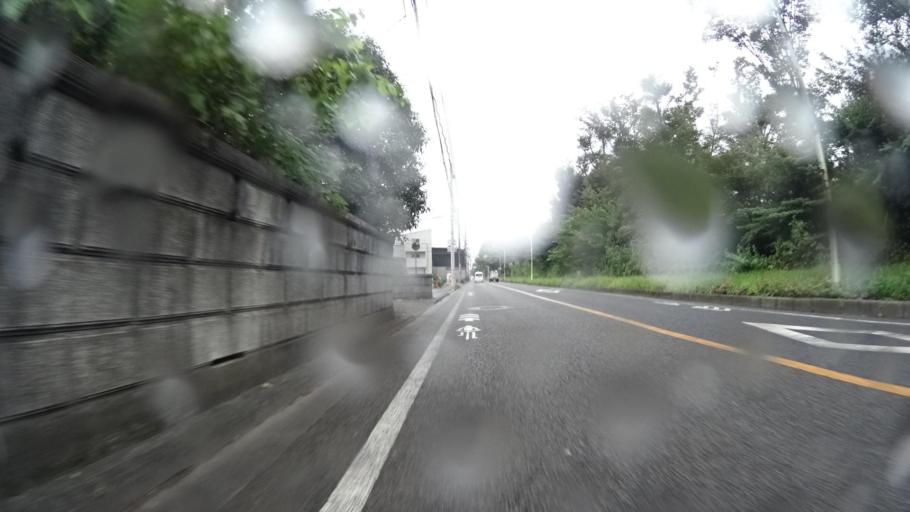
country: JP
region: Tokyo
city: Kokubunji
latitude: 35.7155
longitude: 139.4850
